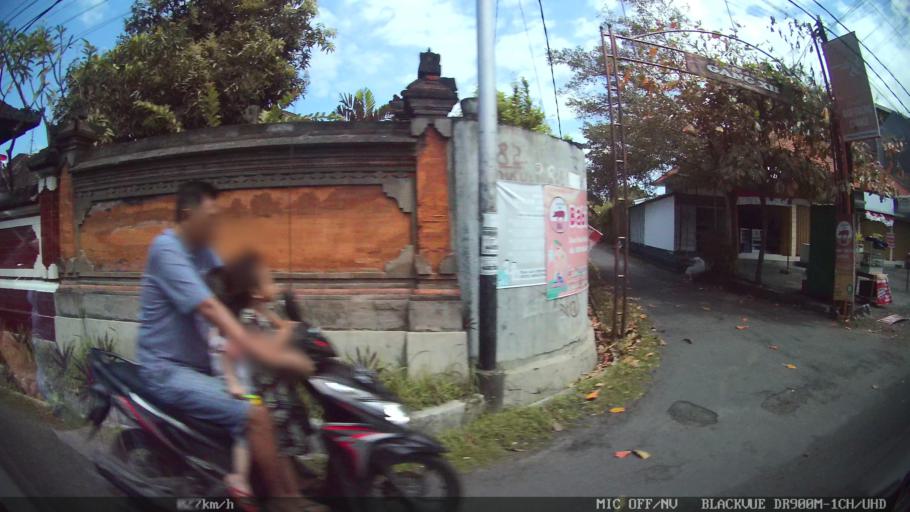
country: ID
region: Bali
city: Karyadharma
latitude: -8.6782
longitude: 115.2028
